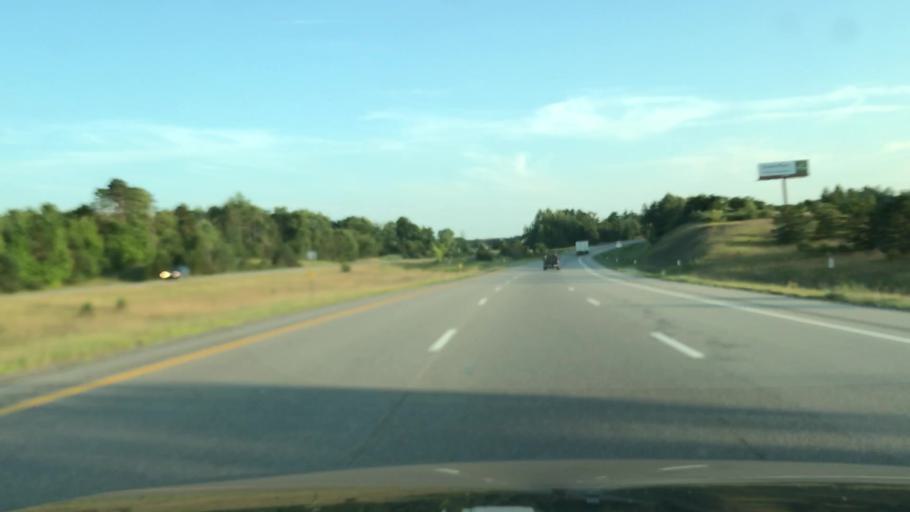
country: US
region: Michigan
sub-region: Osceola County
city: Reed City
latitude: 43.8802
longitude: -85.5282
